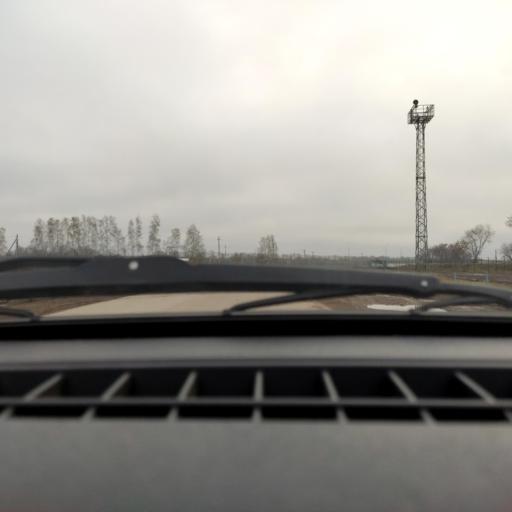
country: RU
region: Bashkortostan
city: Chishmy
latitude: 54.5763
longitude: 55.3512
